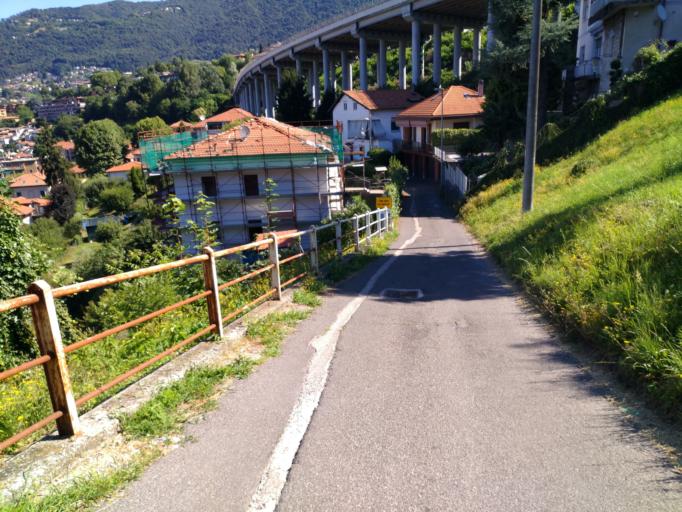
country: CH
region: Ticino
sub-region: Mendrisio District
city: Chiasso
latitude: 45.8315
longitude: 9.0402
